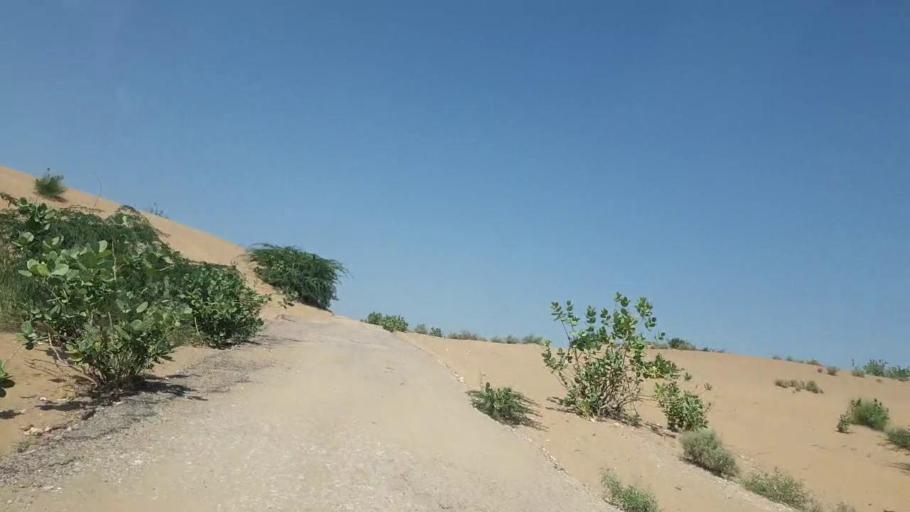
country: PK
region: Sindh
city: Chor
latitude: 25.3504
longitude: 70.3458
